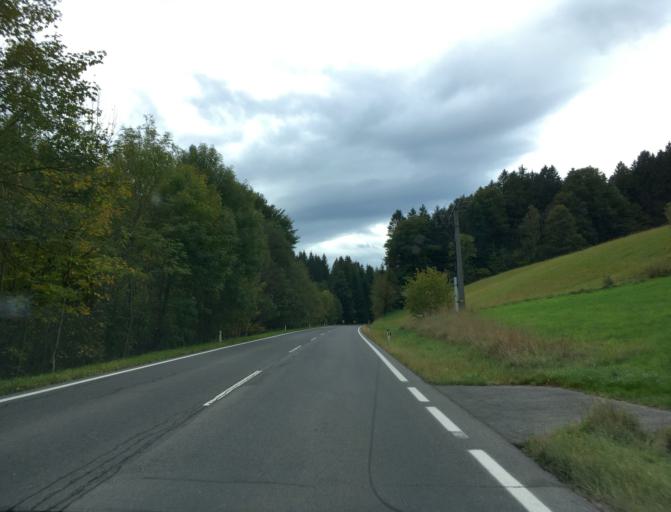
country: AT
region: Lower Austria
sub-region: Politischer Bezirk Neunkirchen
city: Thomasberg
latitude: 47.5598
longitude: 16.1430
